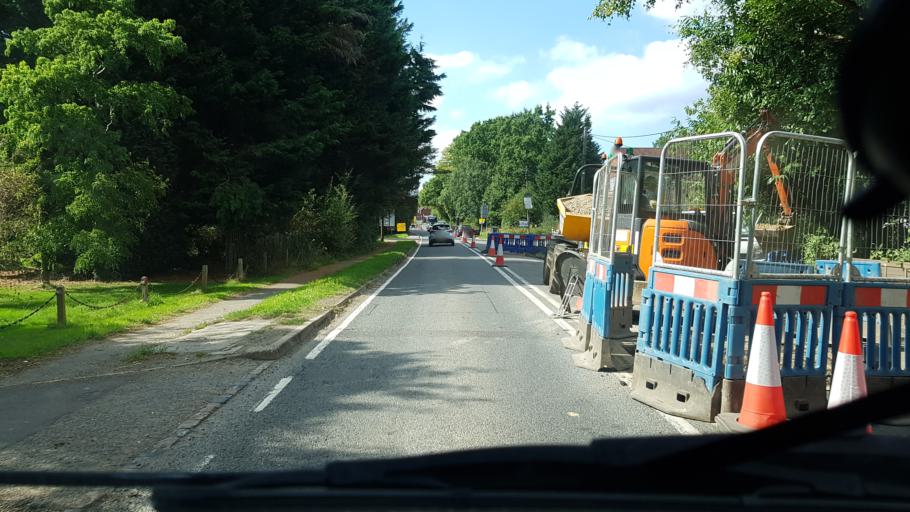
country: GB
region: England
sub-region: Surrey
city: Cranleigh
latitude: 51.1067
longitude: -0.5132
